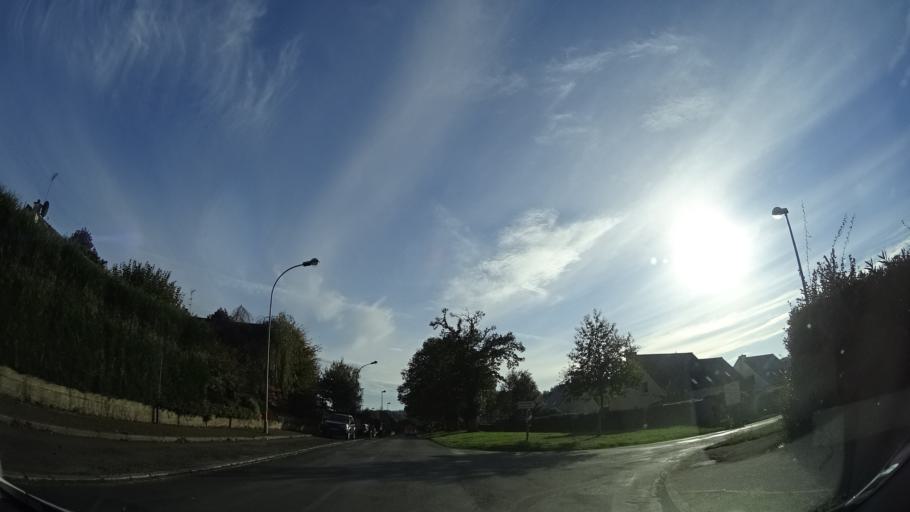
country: FR
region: Brittany
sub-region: Departement d'Ille-et-Vilaine
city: Geveze
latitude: 48.2170
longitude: -1.7911
